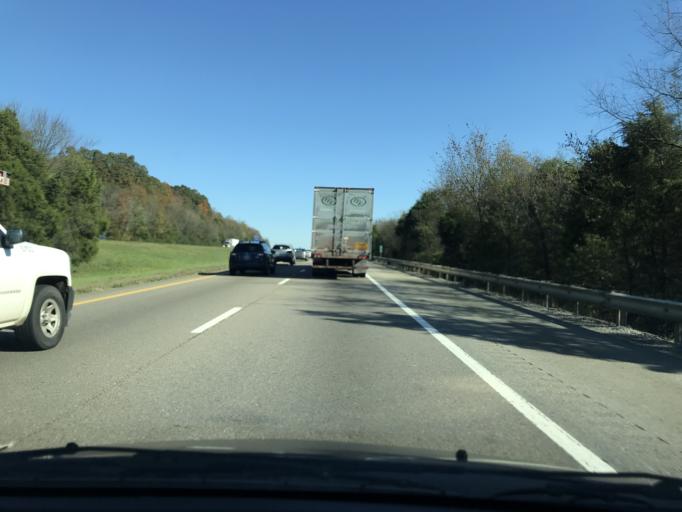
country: US
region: Tennessee
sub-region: Loudon County
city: Loudon
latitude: 35.7435
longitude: -84.3847
